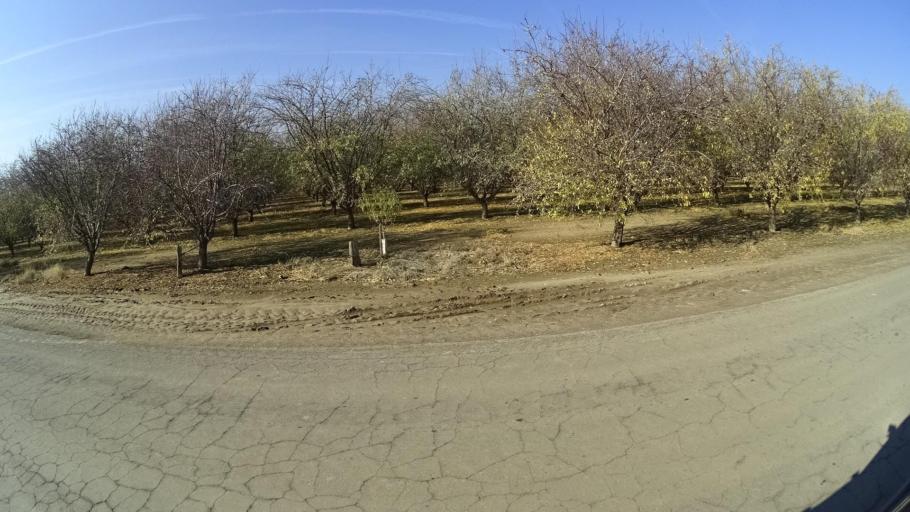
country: US
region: California
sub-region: Kern County
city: Weedpatch
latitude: 35.2008
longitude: -118.8962
